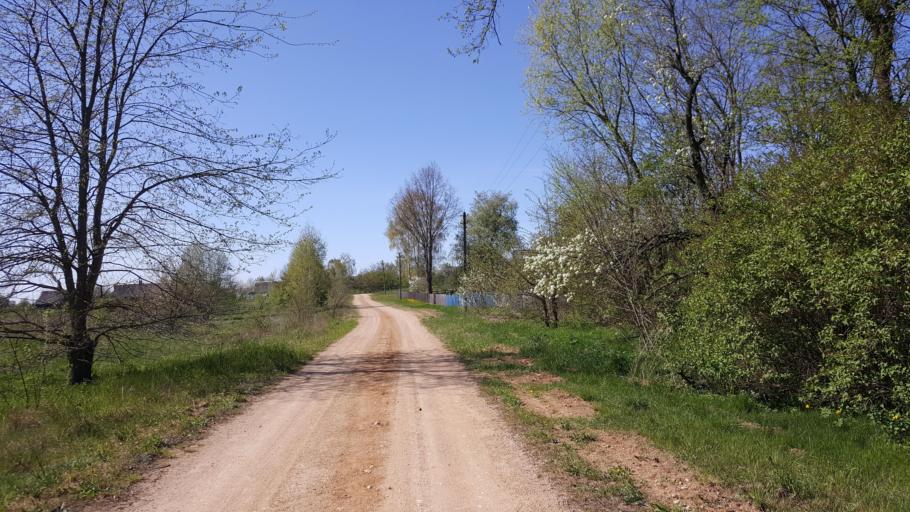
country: BY
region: Brest
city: Kamyanyets
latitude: 52.4506
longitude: 23.8923
